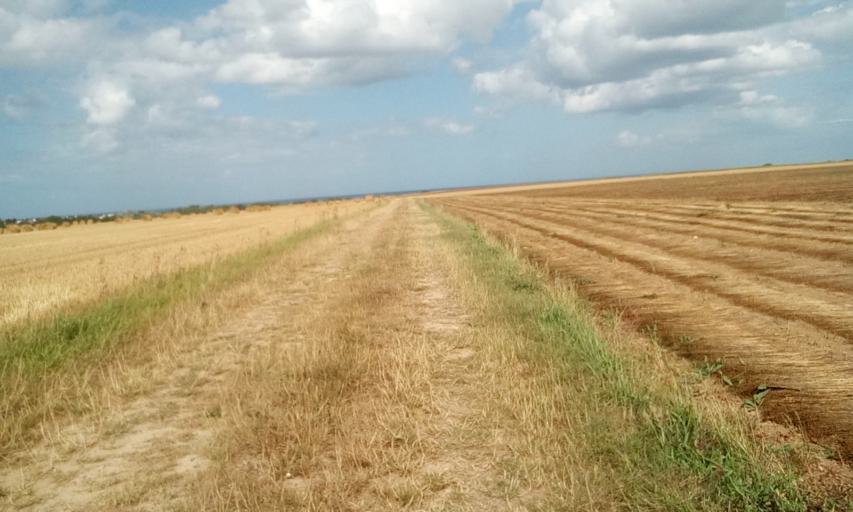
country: FR
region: Lower Normandy
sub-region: Departement du Calvados
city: Ver-sur-Mer
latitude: 49.3280
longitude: -0.5232
